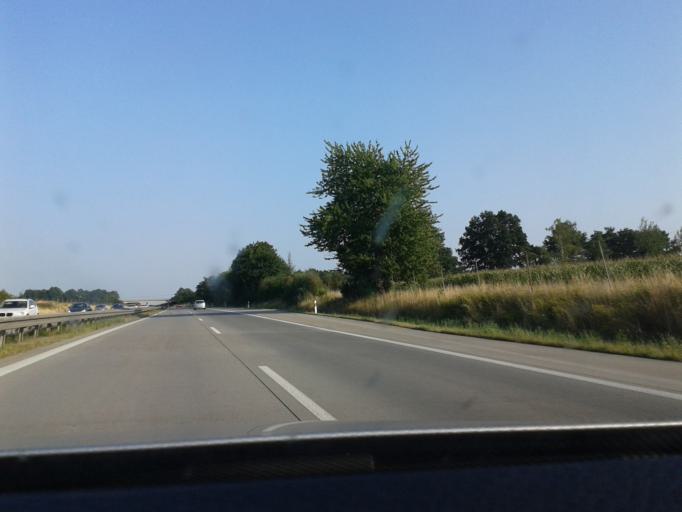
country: DE
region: Saxony
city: Grimma
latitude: 51.2725
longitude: 12.6752
